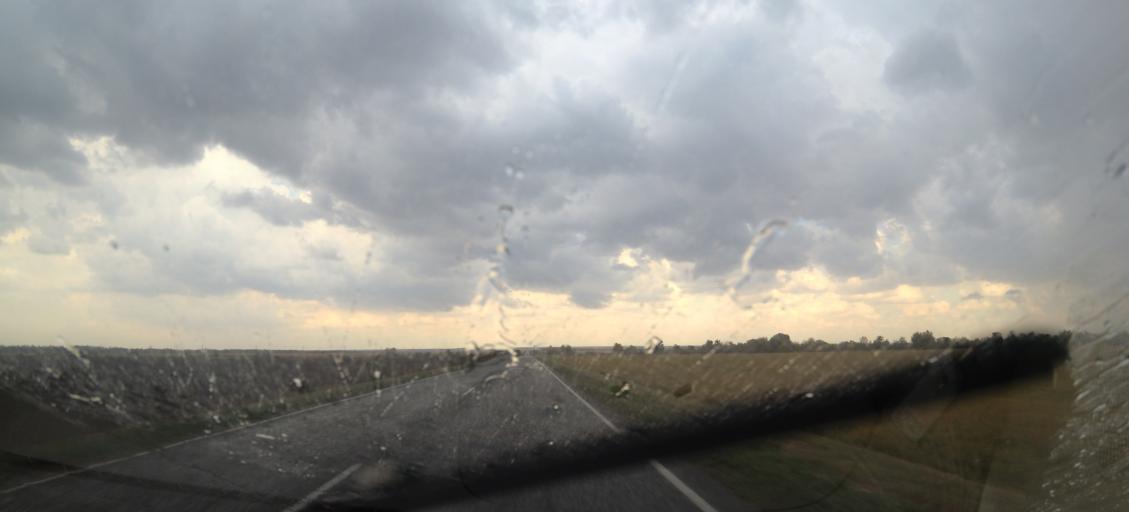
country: RU
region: Rostov
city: Orlovskiy
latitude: 46.8717
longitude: 41.9831
